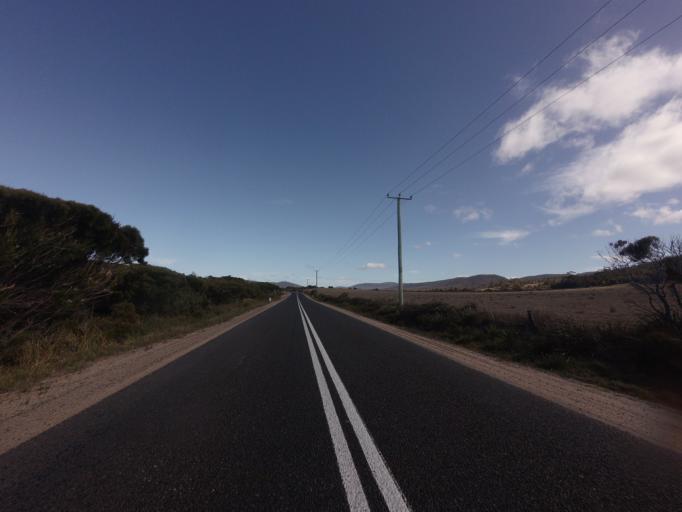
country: AU
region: Tasmania
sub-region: Break O'Day
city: St Helens
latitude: -41.8052
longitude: 148.2629
